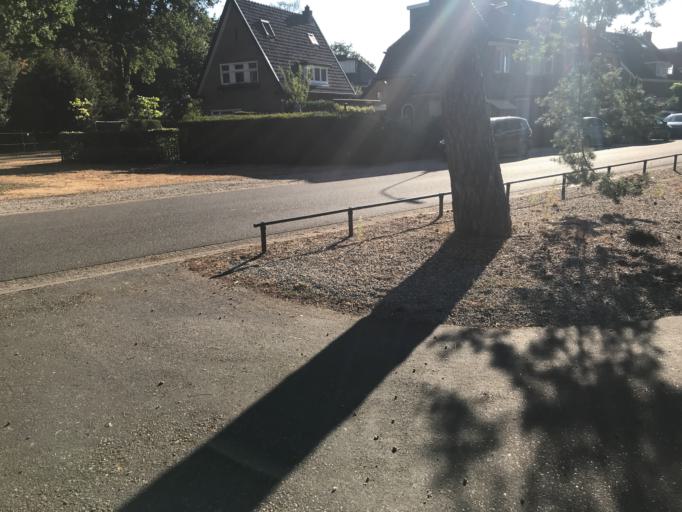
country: NL
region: Gelderland
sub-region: Gemeente Apeldoorn
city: Apeldoorn
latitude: 52.2161
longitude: 5.9372
